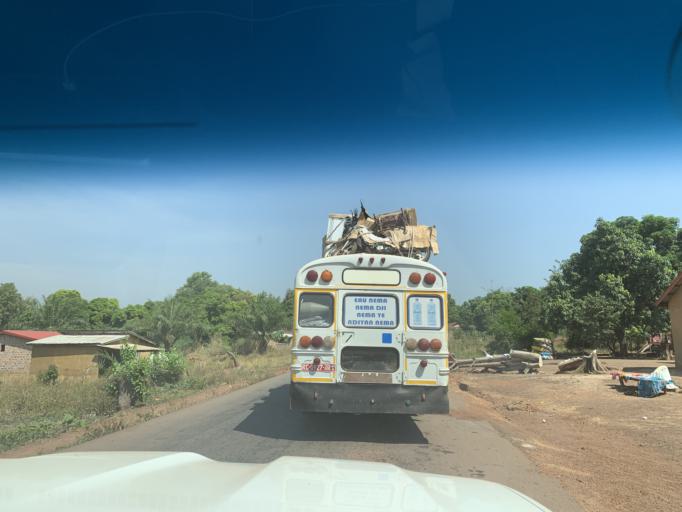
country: GN
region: Kindia
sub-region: Kindia
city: Kindia
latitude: 10.0068
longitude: -12.6943
